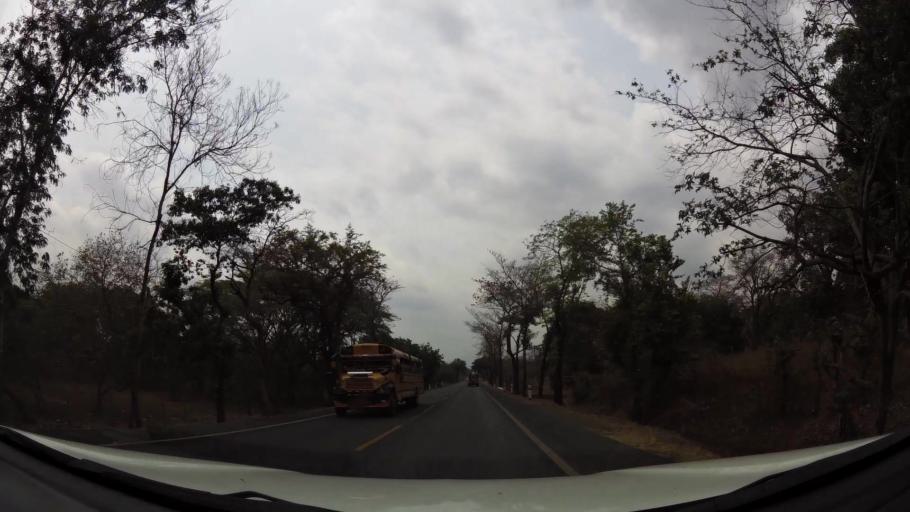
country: NI
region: Leon
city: Telica
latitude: 12.4884
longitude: -86.8611
